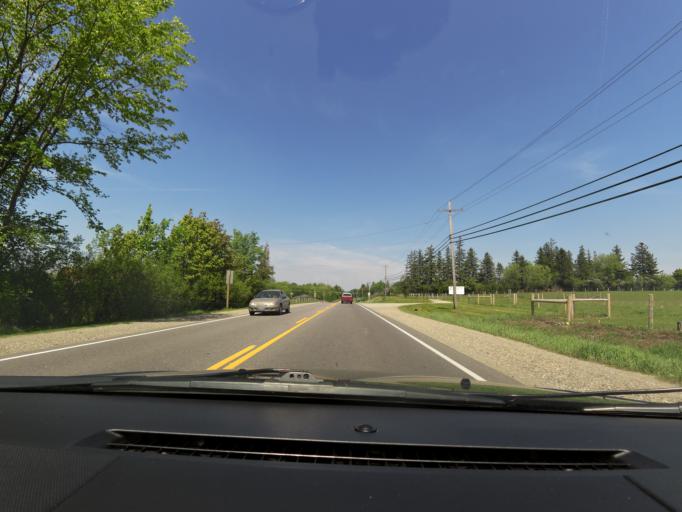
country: CA
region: Ontario
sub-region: Wellington County
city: Guelph
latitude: 43.5704
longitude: -80.1987
